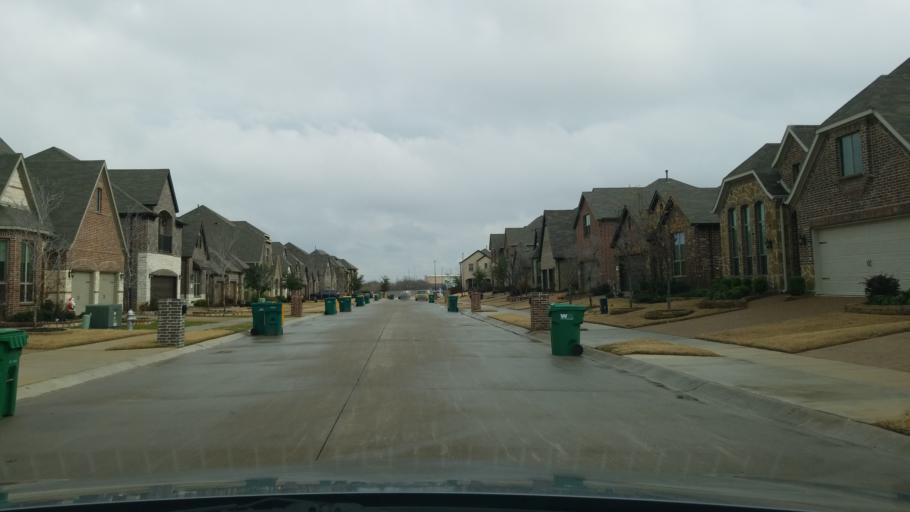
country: US
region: Texas
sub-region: Denton County
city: Lewisville
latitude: 33.0466
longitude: -97.0175
